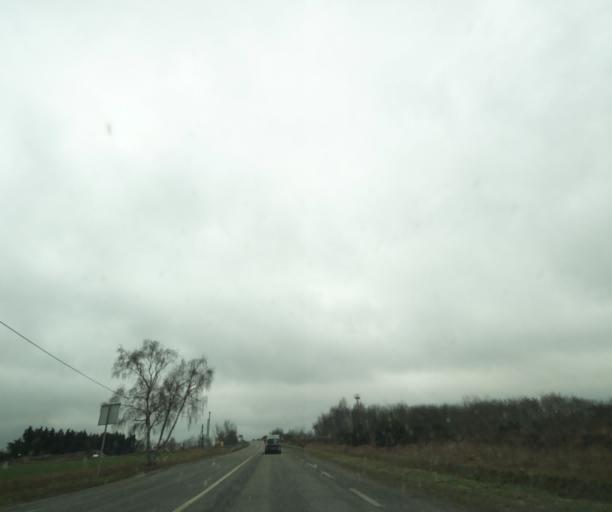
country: FR
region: Ile-de-France
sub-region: Departement de l'Essonne
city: Champlan
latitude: 48.7159
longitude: 2.2820
